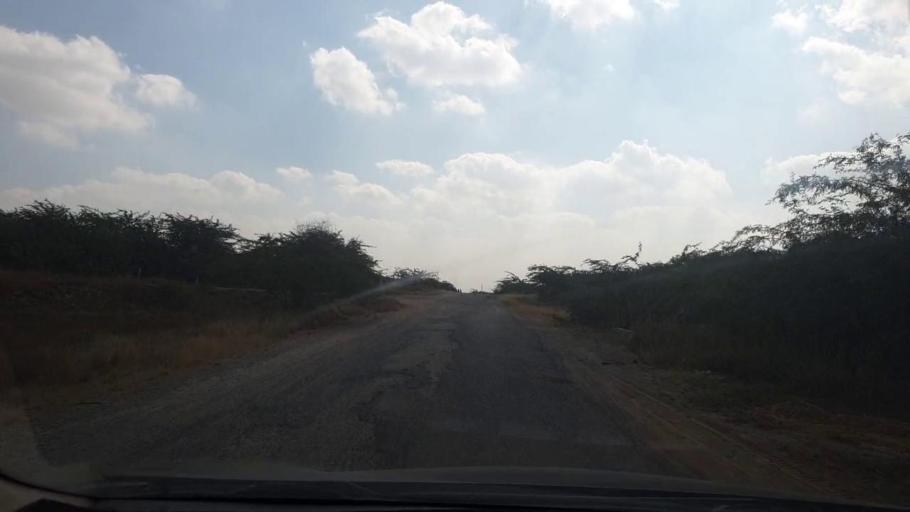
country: PK
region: Sindh
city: Malir Cantonment
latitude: 25.0250
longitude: 67.3525
